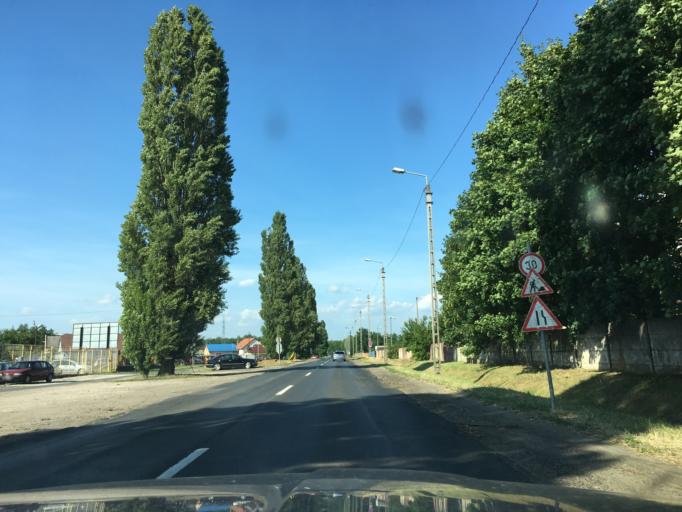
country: HU
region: Hajdu-Bihar
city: Debrecen
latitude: 47.5553
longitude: 21.6679
